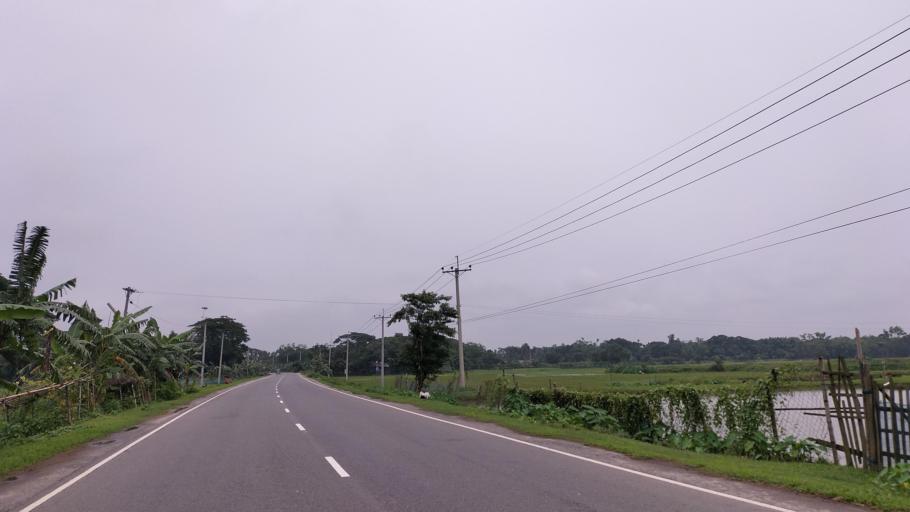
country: BD
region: Dhaka
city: Netrakona
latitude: 24.8520
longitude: 90.6203
